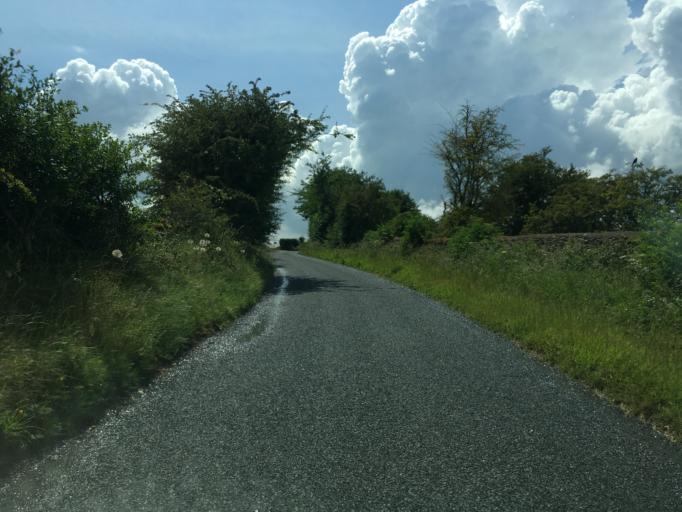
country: GB
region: England
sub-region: Wiltshire
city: Luckington
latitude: 51.6189
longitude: -2.2277
